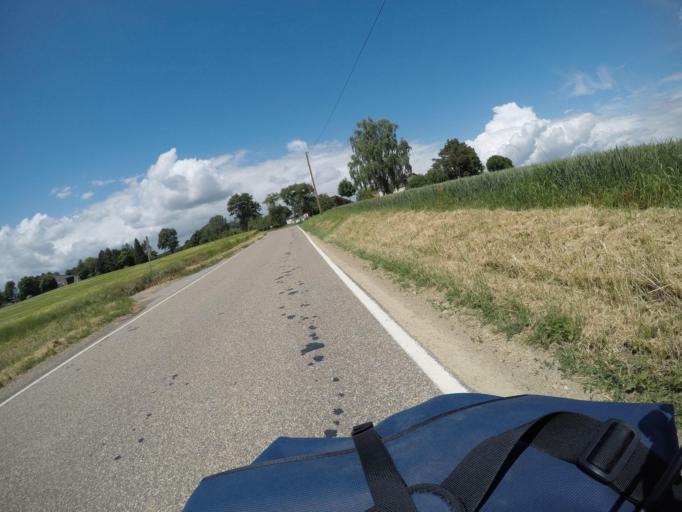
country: DE
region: Baden-Wuerttemberg
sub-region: Regierungsbezirk Stuttgart
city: Ittlingen
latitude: 49.1873
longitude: 8.9082
